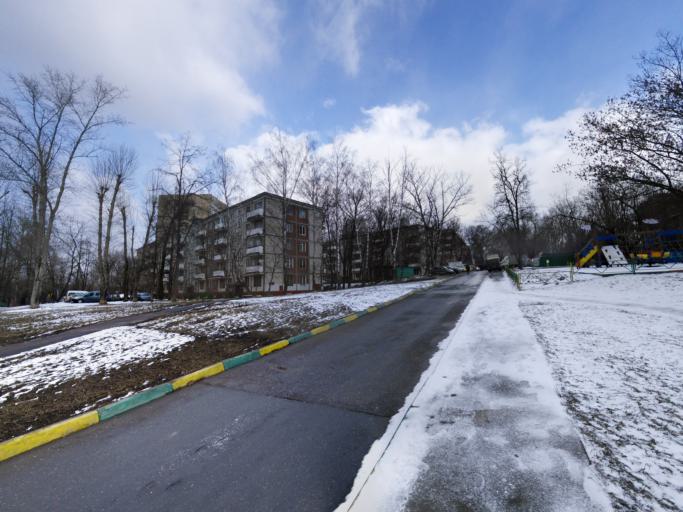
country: RU
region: Moscow
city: Davydkovo
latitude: 55.7309
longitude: 37.4520
